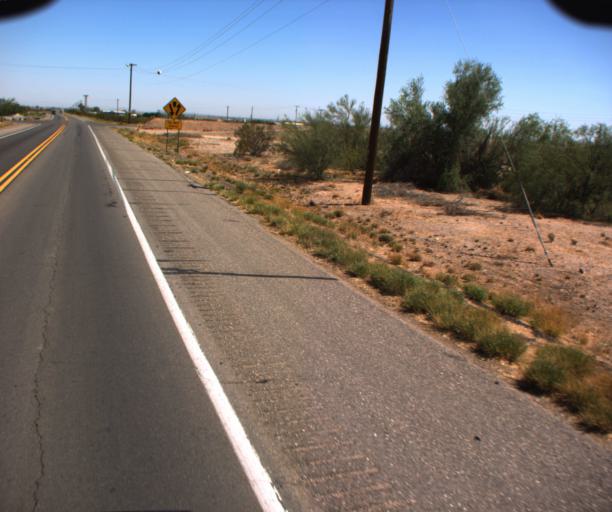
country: US
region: Arizona
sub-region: Pinal County
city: Maricopa
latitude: 32.8781
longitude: -112.0493
